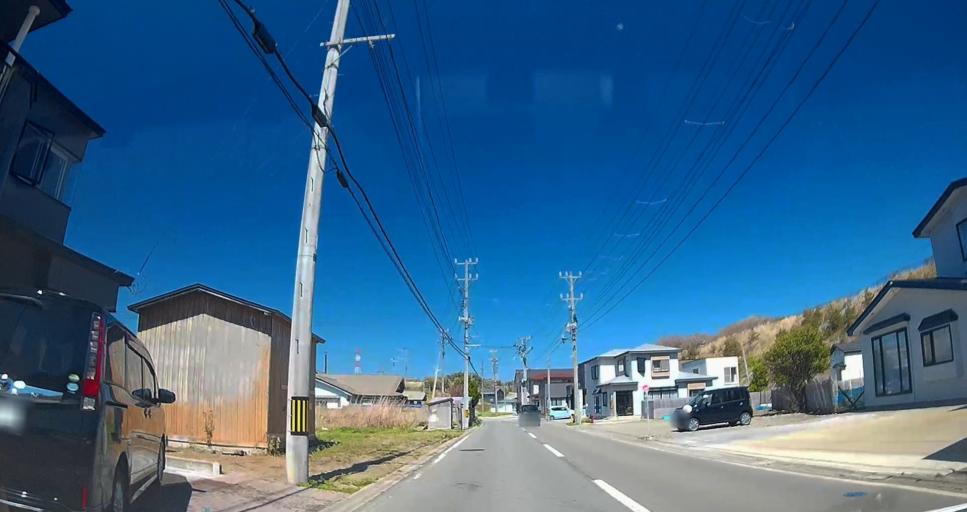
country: JP
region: Hokkaido
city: Hakodate
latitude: 41.5022
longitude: 140.9103
